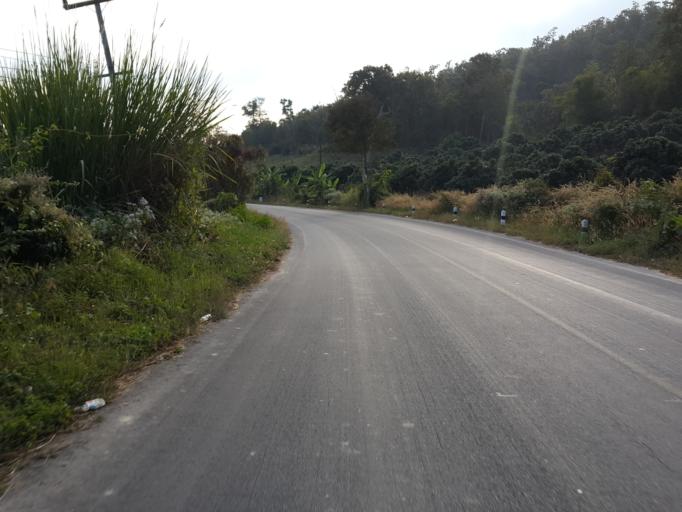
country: TH
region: Lamphun
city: Thung Hua Chang
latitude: 18.0321
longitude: 99.0285
